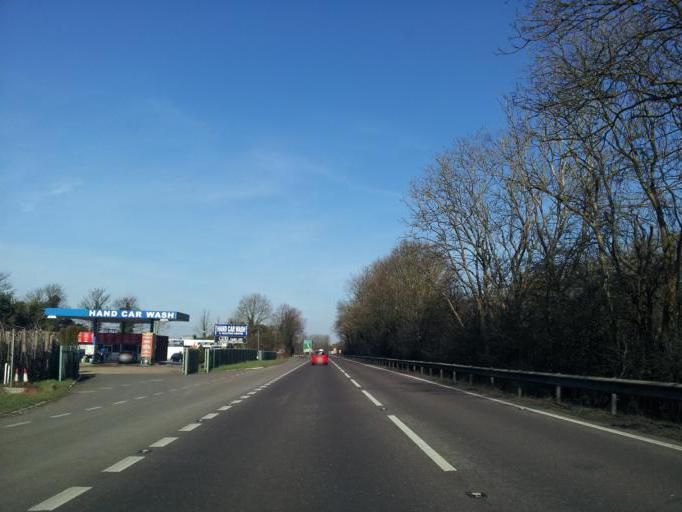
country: GB
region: England
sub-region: Cambridgeshire
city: Little Paxton
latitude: 52.2585
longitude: -0.2636
